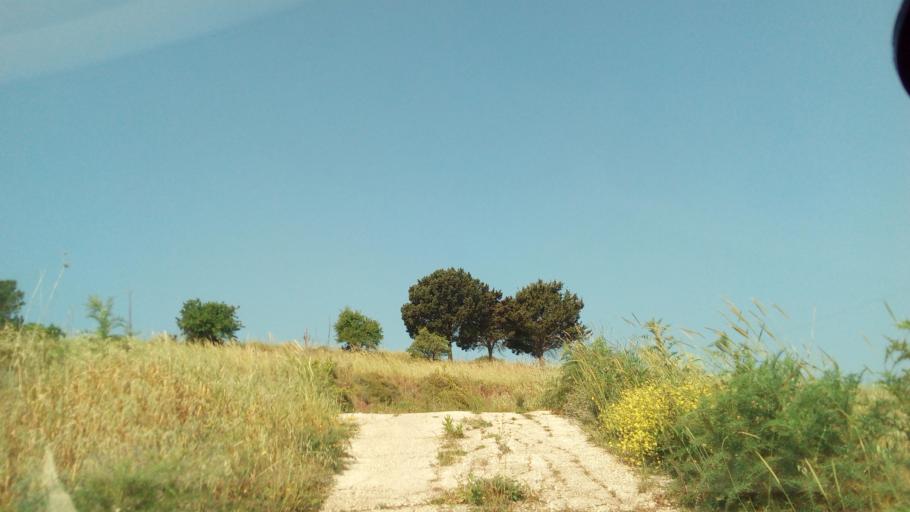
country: CY
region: Pafos
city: Polis
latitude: 34.9779
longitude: 32.3765
